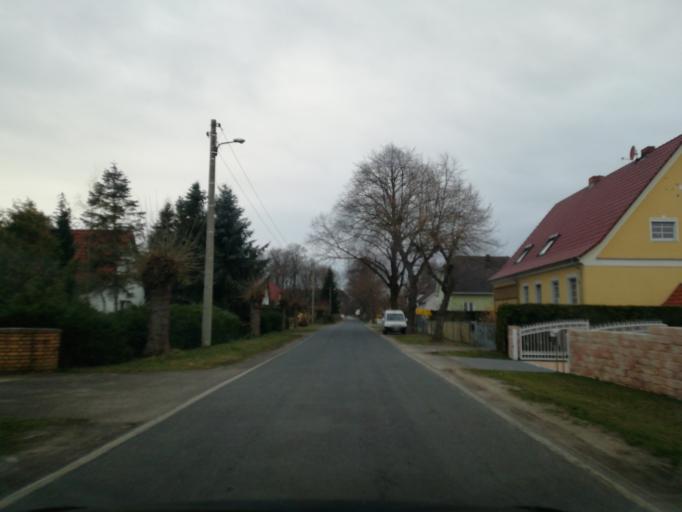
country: DE
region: Brandenburg
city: Vetschau
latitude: 51.7413
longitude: 14.1018
